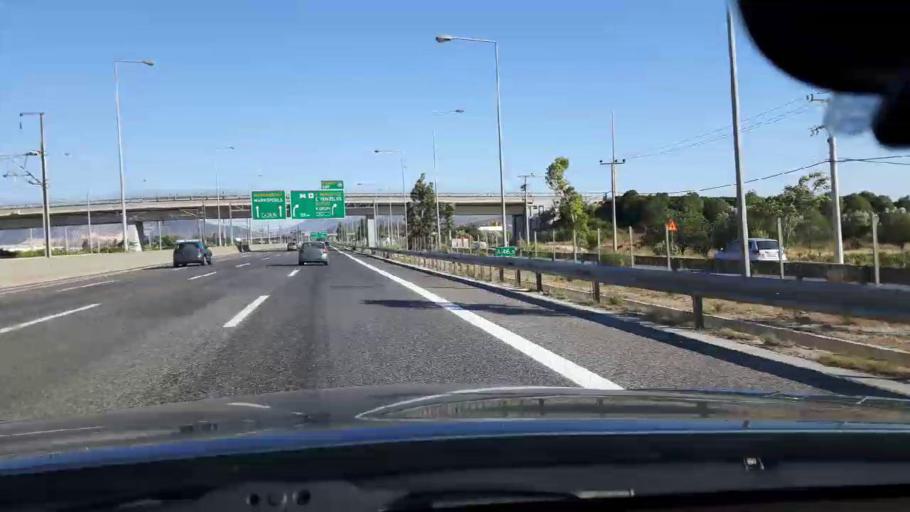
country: GR
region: Attica
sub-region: Nomarchia Anatolikis Attikis
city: Koropi
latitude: 37.9090
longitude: 23.8986
